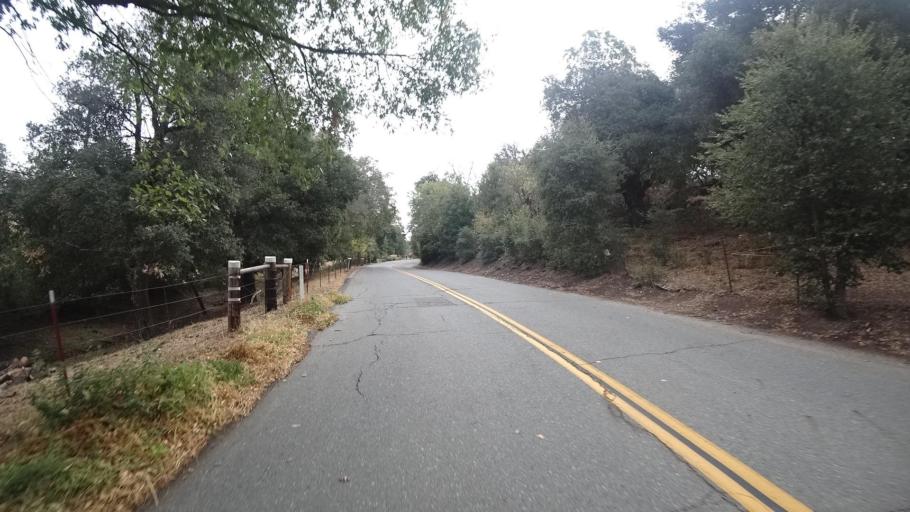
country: US
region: California
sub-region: San Diego County
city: Julian
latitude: 33.0463
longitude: -116.6113
